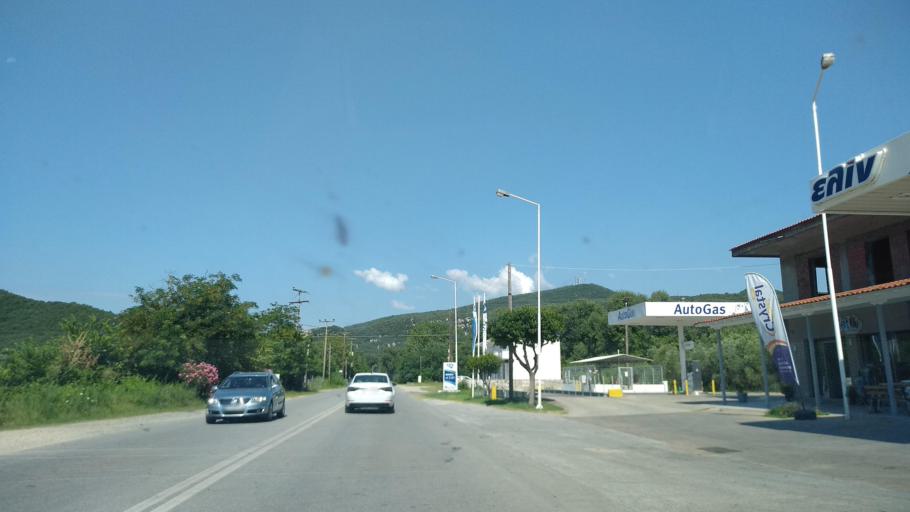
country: GR
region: Central Macedonia
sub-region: Nomos Thessalonikis
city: Stavros
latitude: 40.6687
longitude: 23.6759
